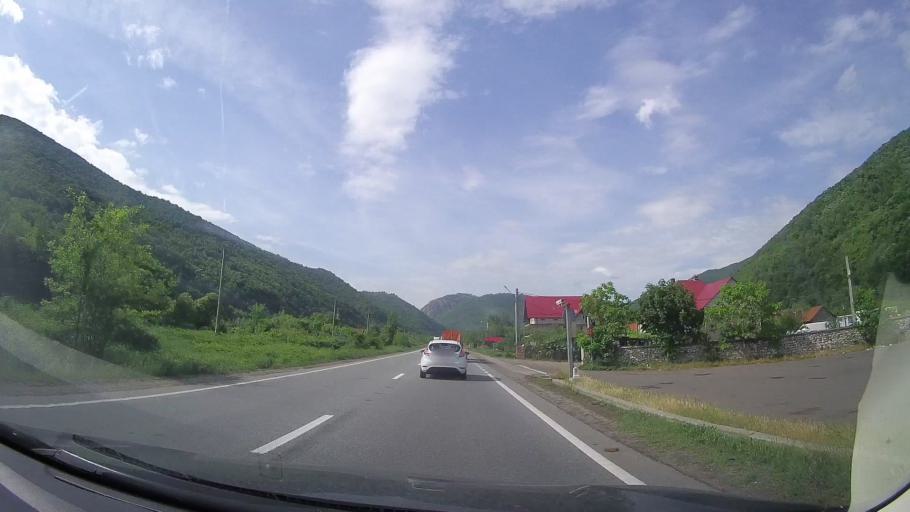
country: RO
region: Caras-Severin
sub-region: Oras Baile Herculane
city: Baile Herculane
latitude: 44.8704
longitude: 22.3872
